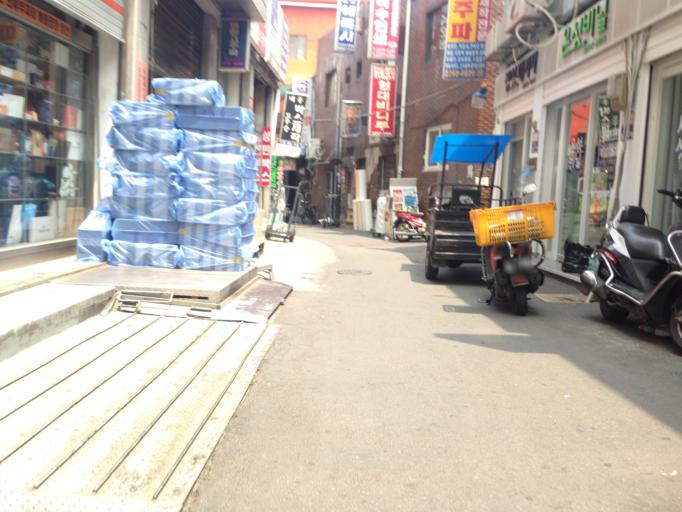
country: KR
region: Seoul
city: Seoul
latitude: 37.5671
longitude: 127.0003
